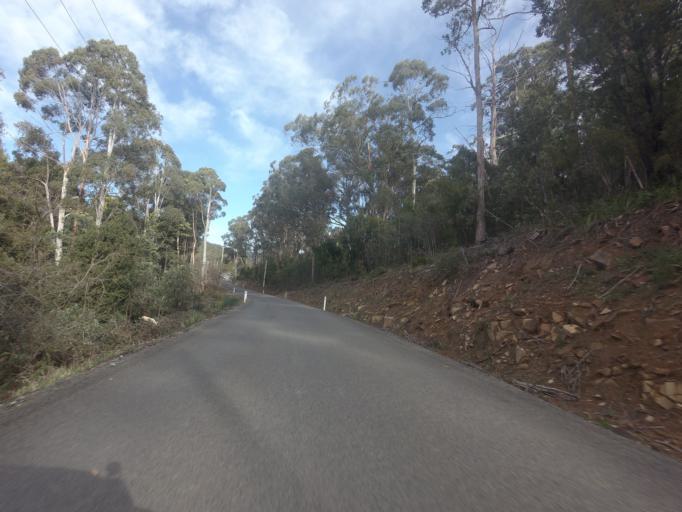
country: AU
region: Tasmania
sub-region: Kingborough
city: Margate
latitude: -42.9862
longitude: 147.1932
